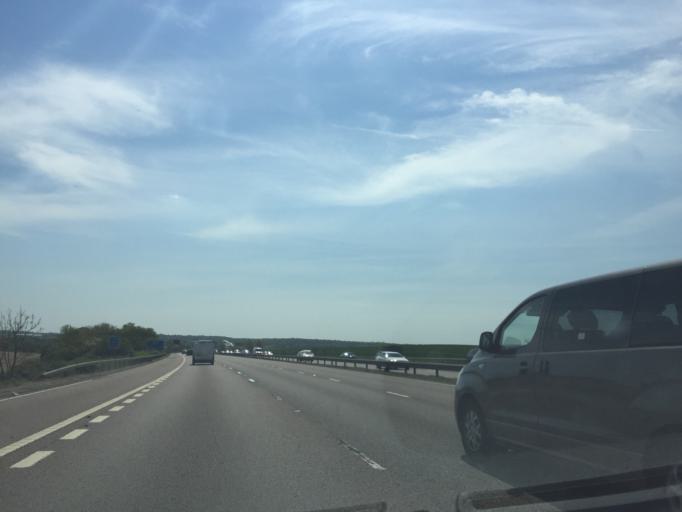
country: GB
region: England
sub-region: Essex
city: Epping
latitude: 51.7359
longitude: 0.1373
